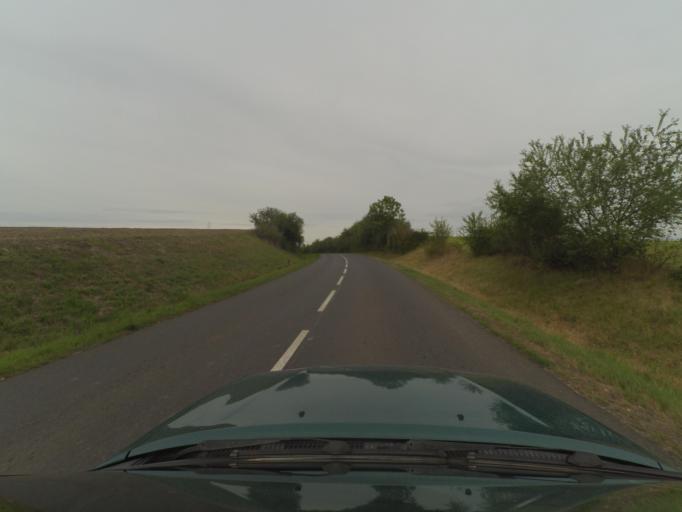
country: CZ
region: Ustecky
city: Peruc
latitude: 50.3976
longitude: 13.9280
